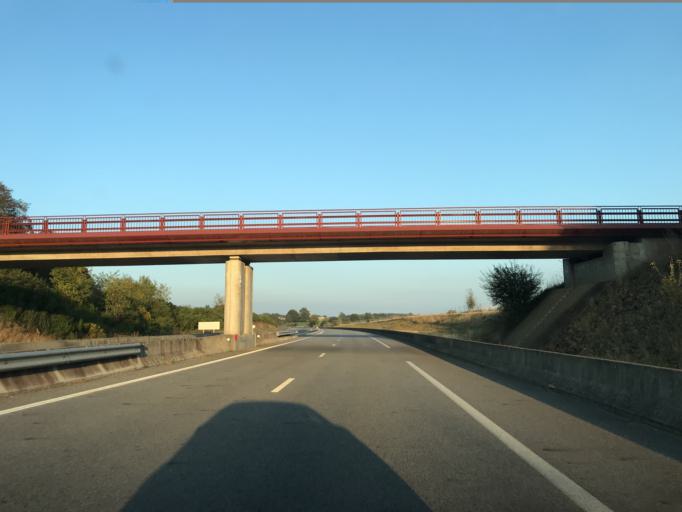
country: FR
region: Lower Normandy
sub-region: Departement de l'Orne
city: Sees
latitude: 48.4858
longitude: 0.2805
